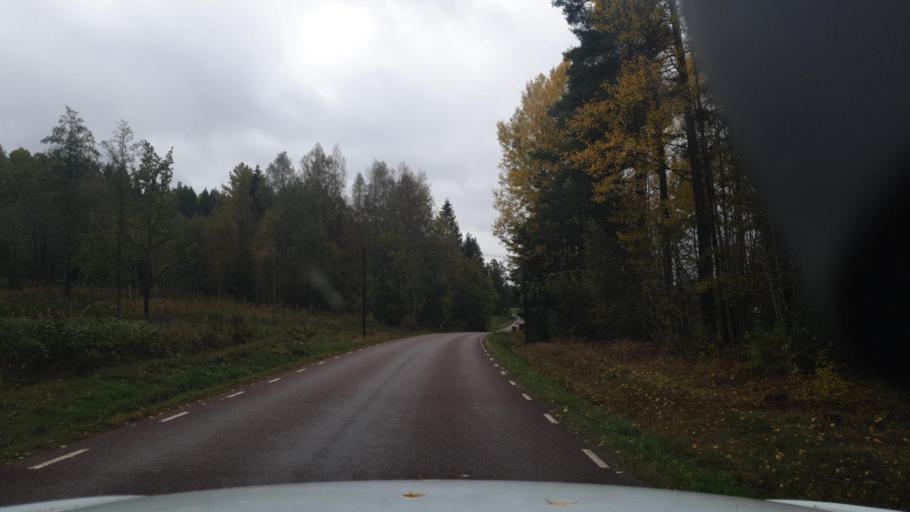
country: SE
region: Vaermland
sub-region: Grums Kommun
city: Grums
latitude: 59.4052
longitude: 13.0714
